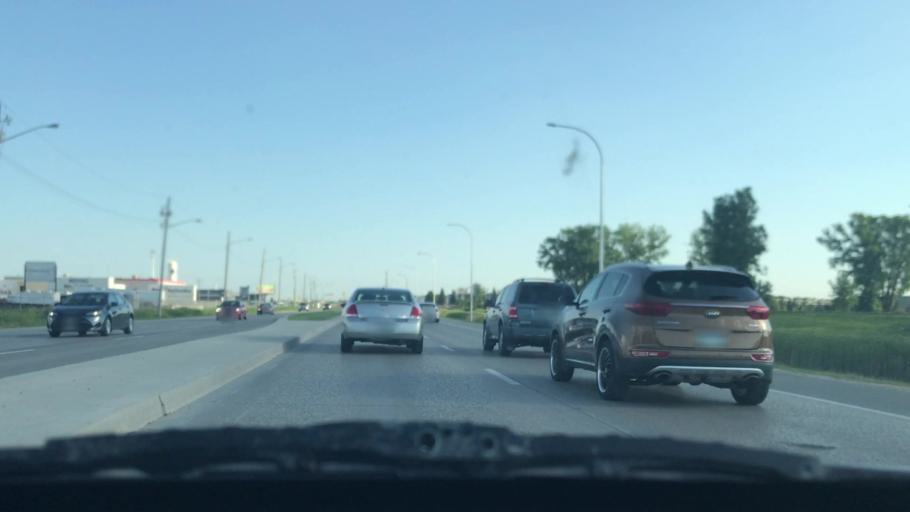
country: CA
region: Manitoba
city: Winnipeg
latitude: 49.8356
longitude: -97.2094
